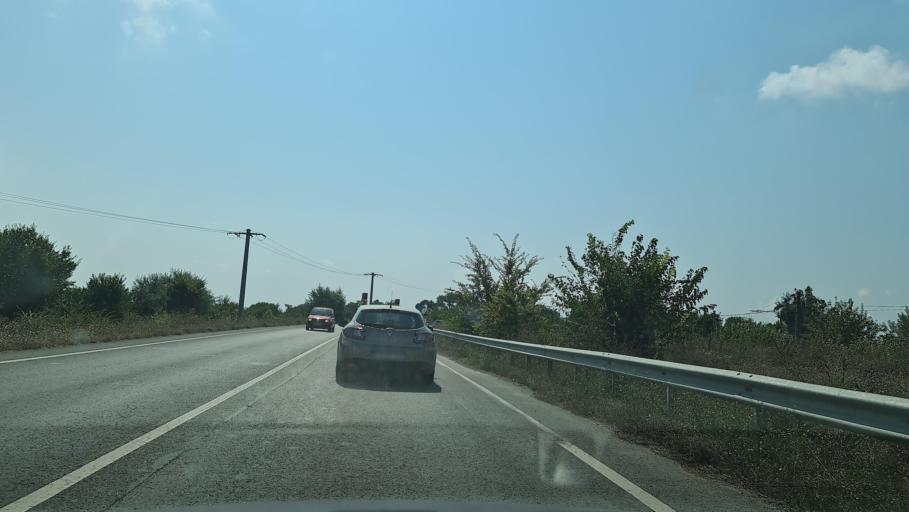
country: RO
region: Constanta
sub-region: Comuna Agigea
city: Agigea
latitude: 44.0917
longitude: 28.6393
